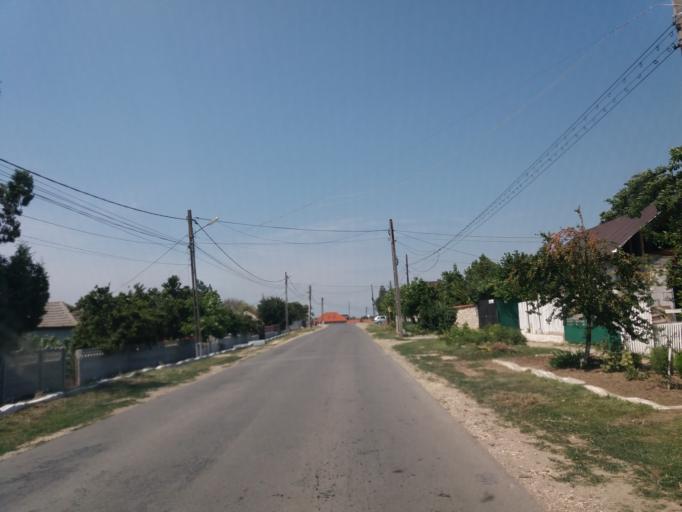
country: RO
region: Constanta
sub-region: Comuna Corbu
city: Corbu
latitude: 44.4042
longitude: 28.6615
